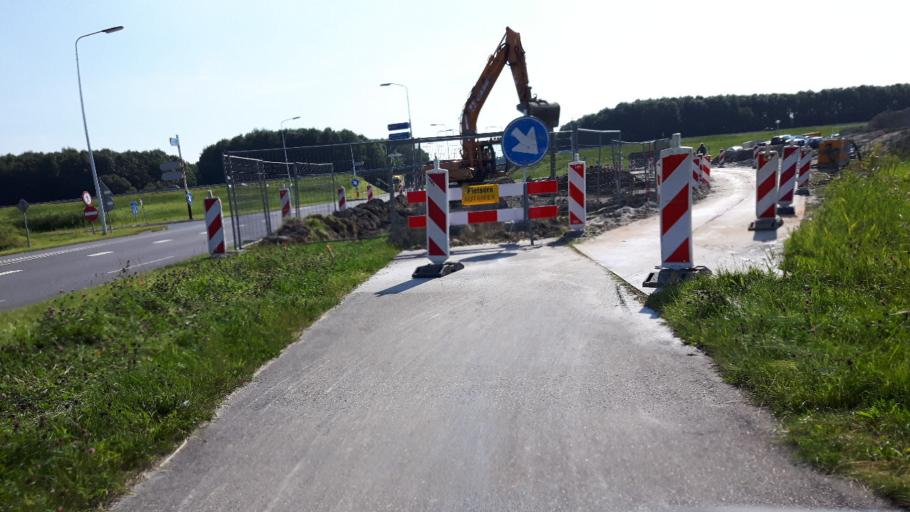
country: NL
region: Friesland
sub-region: Gemeente Franekeradeel
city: Franeker
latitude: 53.2026
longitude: 5.5417
